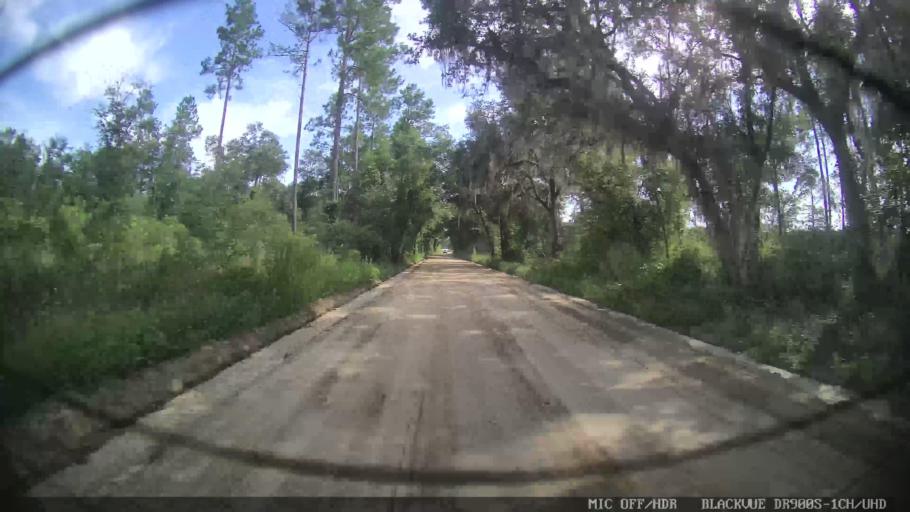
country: US
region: Georgia
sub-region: Echols County
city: Statenville
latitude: 30.6208
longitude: -83.2007
